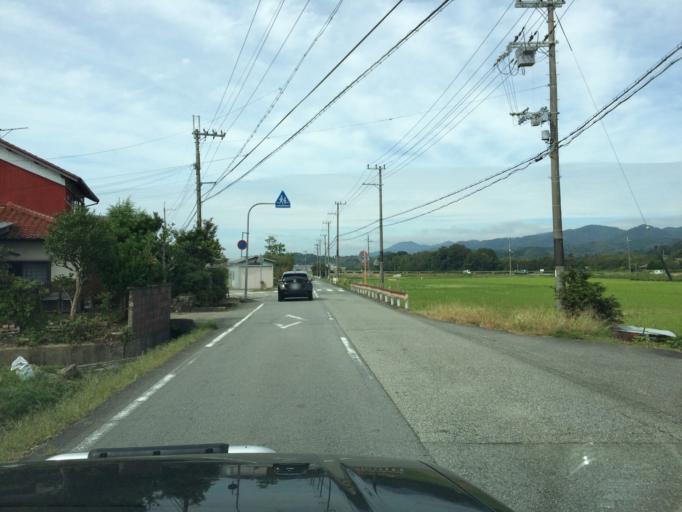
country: JP
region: Hyogo
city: Sasayama
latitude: 35.0692
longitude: 135.2701
